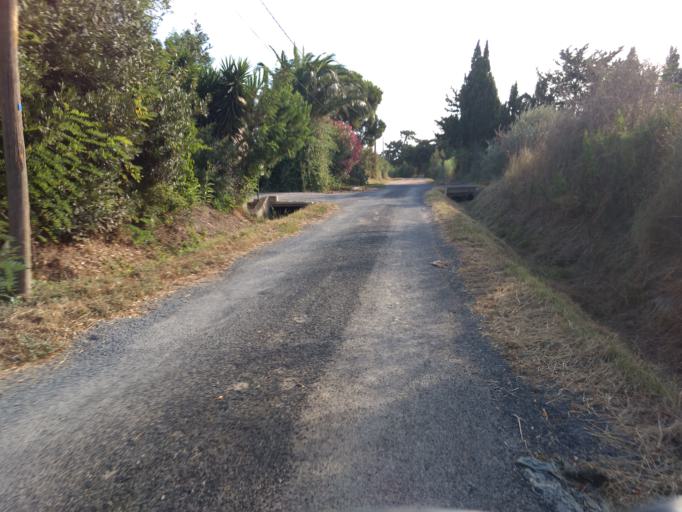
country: FR
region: Languedoc-Roussillon
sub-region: Departement des Pyrenees-Orientales
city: Saint-Laurent-de-la-Salanque
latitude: 42.7785
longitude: 3.0133
